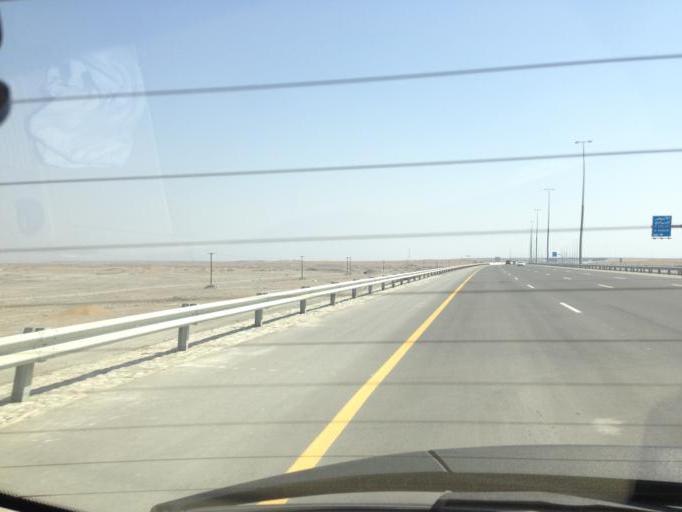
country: OM
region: Al Batinah
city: Barka'
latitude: 23.5699
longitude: 57.7121
